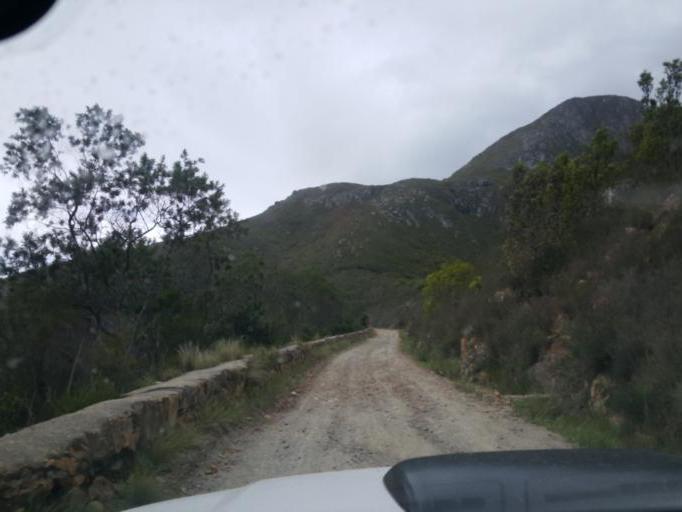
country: ZA
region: Western Cape
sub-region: Eden District Municipality
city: George
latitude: -33.8887
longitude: 22.4269
